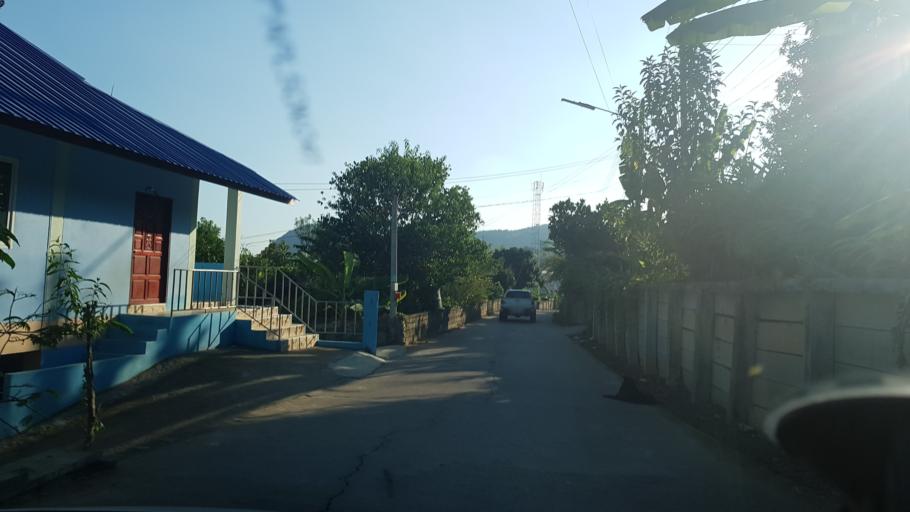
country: TH
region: Chiang Rai
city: Chiang Rai
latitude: 19.9465
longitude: 99.8065
